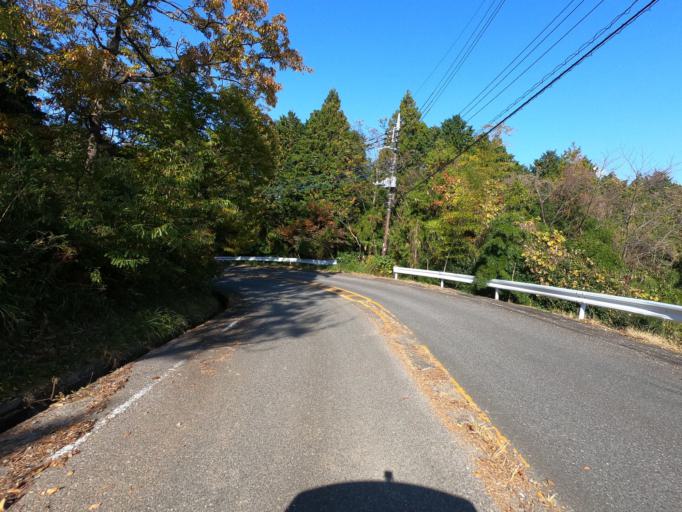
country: JP
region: Ibaraki
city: Tsukuba
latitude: 36.2329
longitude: 140.1278
